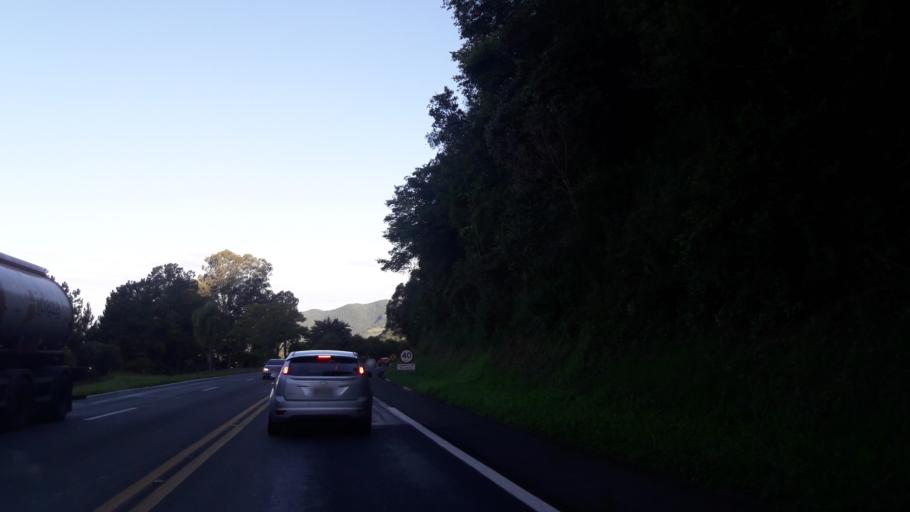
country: BR
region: Parana
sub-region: Prudentopolis
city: Prudentopolis
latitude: -25.3155
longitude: -51.1984
